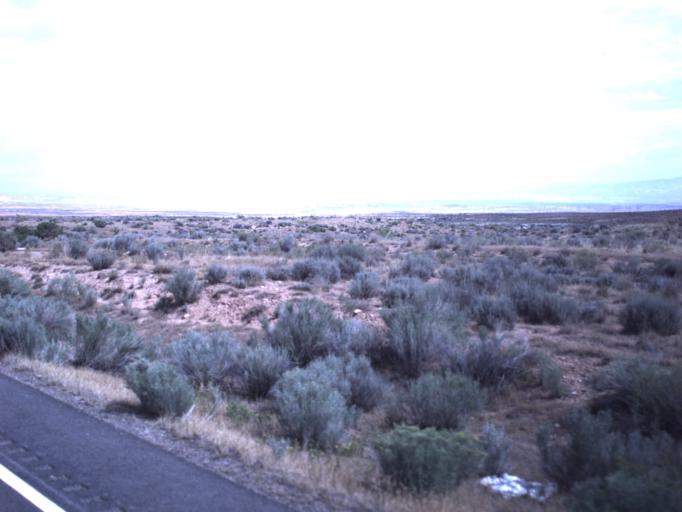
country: US
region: Utah
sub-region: Uintah County
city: Naples
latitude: 40.2314
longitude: -109.4105
